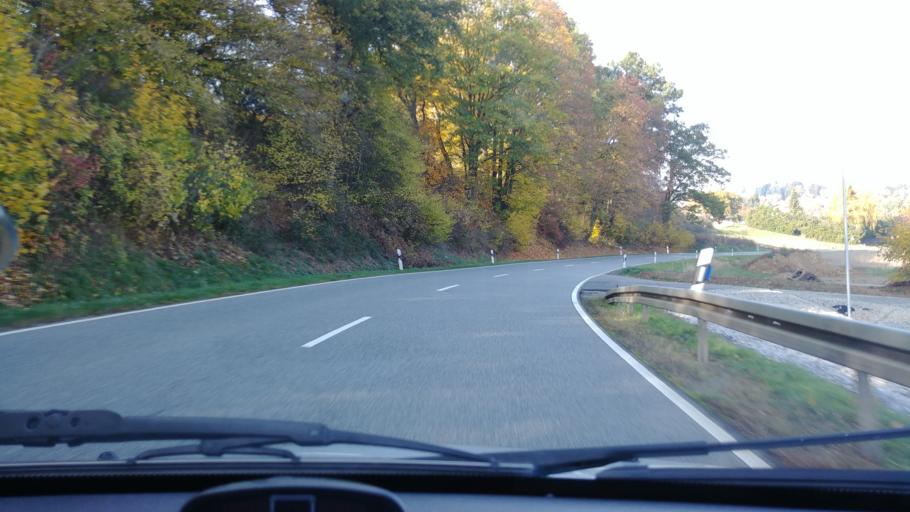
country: DE
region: Rheinland-Pfalz
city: Schiesheim
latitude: 50.2588
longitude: 8.0541
